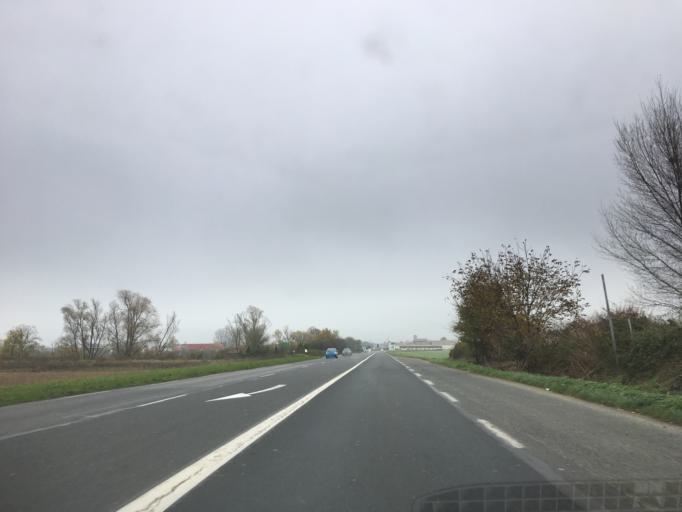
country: FR
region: Ile-de-France
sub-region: Departement de Seine-et-Marne
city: Varennes-sur-Seine
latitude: 48.3609
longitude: 2.9431
